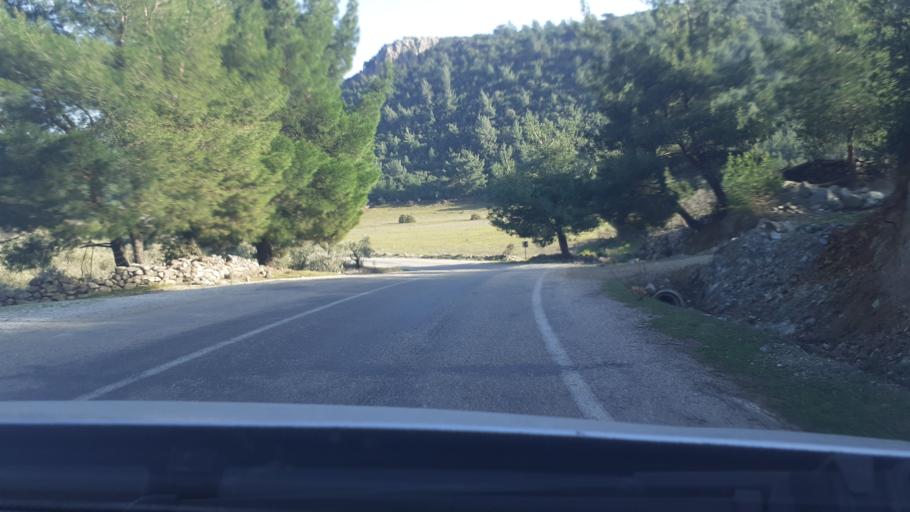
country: TR
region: Hatay
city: Aktepe
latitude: 36.7343
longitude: 36.4687
